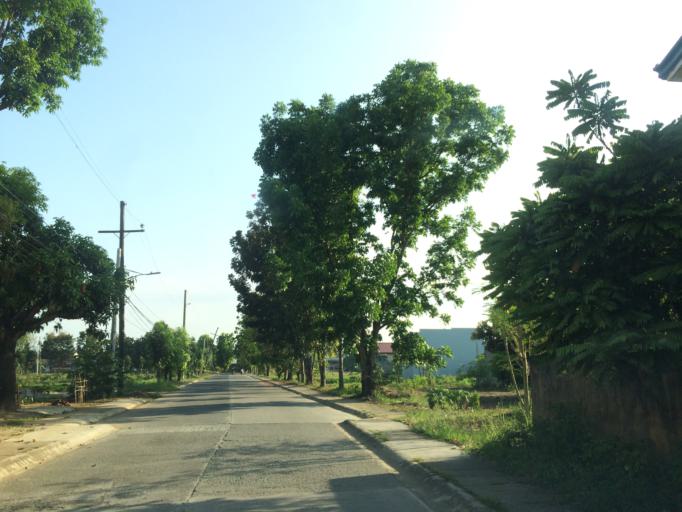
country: PH
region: Calabarzon
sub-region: Province of Rizal
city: San Mateo
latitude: 14.6747
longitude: 121.1227
